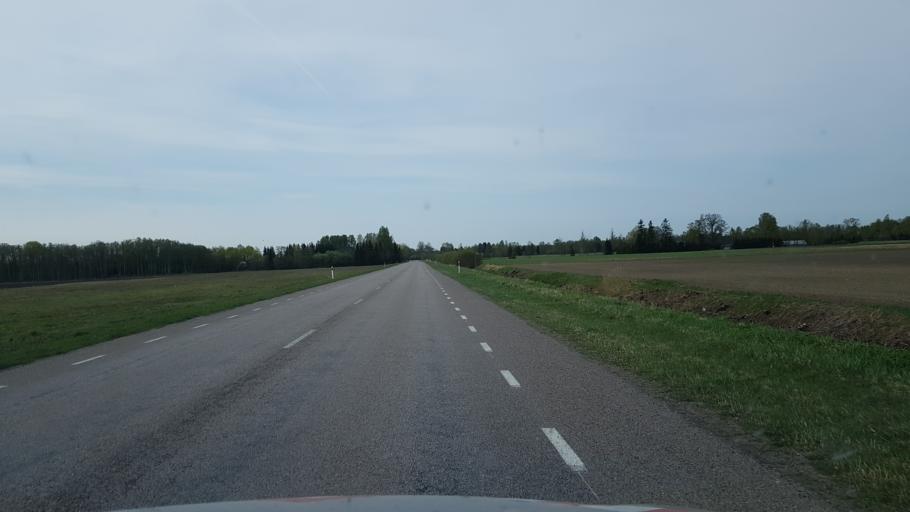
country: EE
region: Paernumaa
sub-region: Audru vald
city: Audru
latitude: 58.3775
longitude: 24.2707
